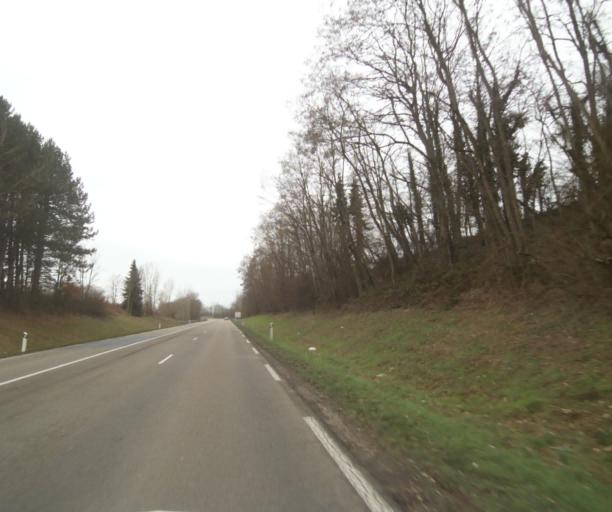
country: FR
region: Champagne-Ardenne
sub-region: Departement de la Haute-Marne
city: Bienville
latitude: 48.5883
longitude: 5.0298
